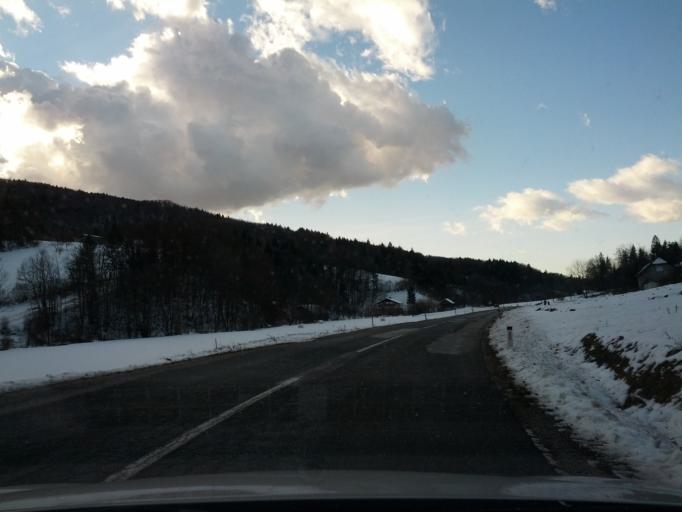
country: SI
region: Litija
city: Litija
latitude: 46.1345
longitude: 14.8259
